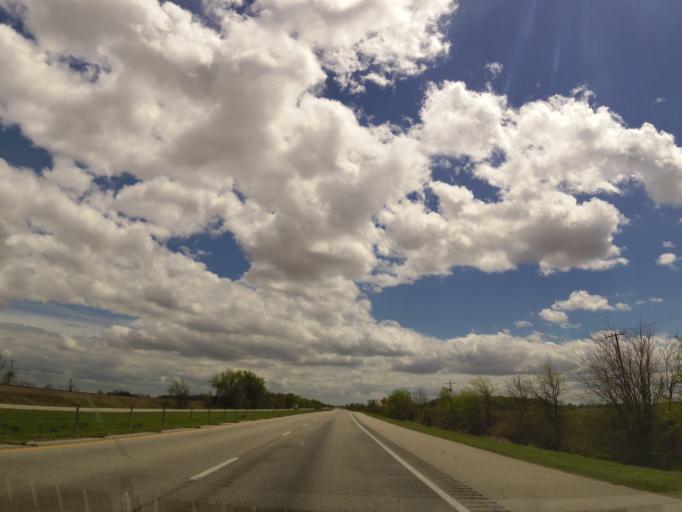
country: US
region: Arkansas
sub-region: Poinsett County
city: Marked Tree
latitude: 35.4438
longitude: -90.3069
